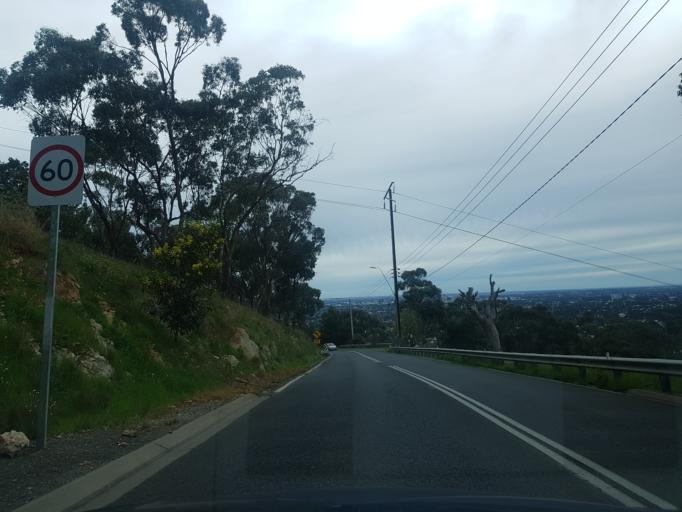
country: AU
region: South Australia
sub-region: Mitcham
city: Mitcham
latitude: -34.9875
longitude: 138.6249
